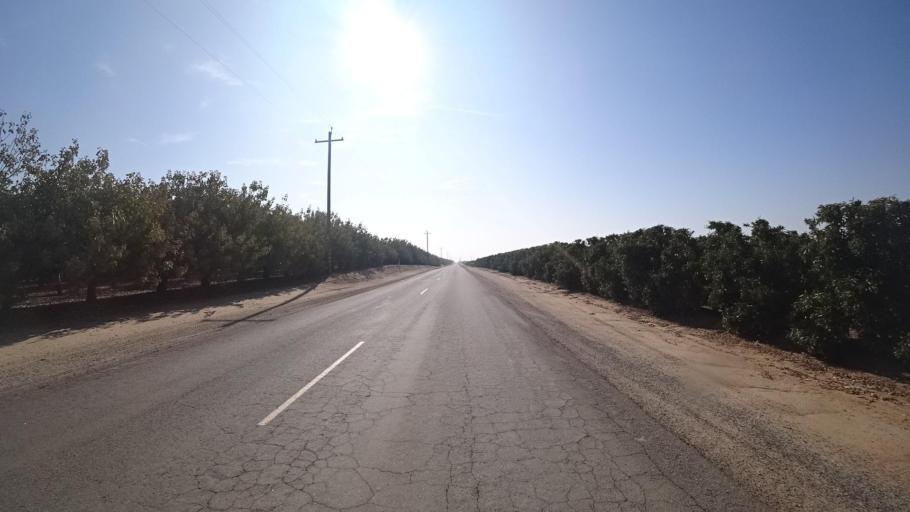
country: US
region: California
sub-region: Kern County
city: McFarland
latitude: 35.6091
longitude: -119.1688
